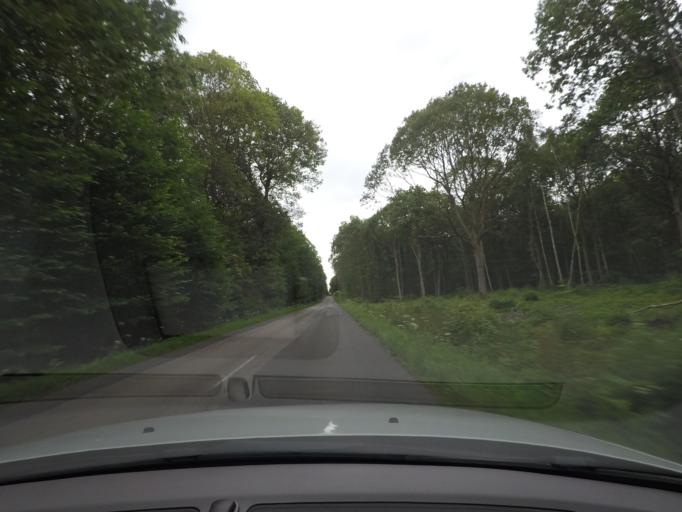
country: FR
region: Haute-Normandie
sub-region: Departement de l'Eure
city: Le Manoir
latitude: 49.3337
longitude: 1.2008
